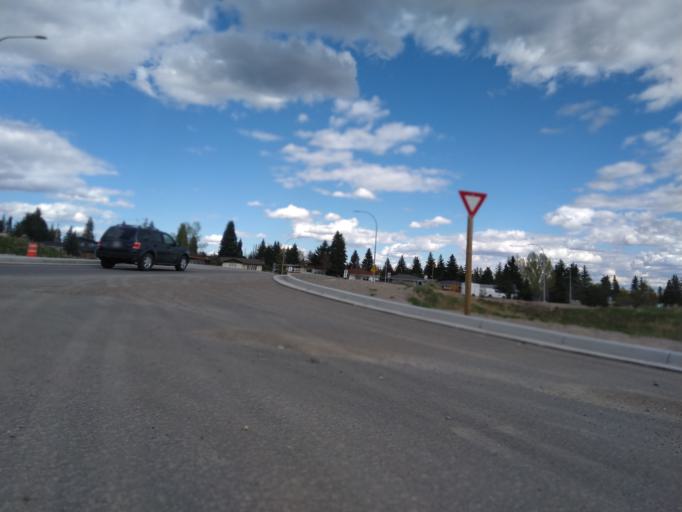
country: CA
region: Alberta
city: Calgary
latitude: 51.0033
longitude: -114.1431
